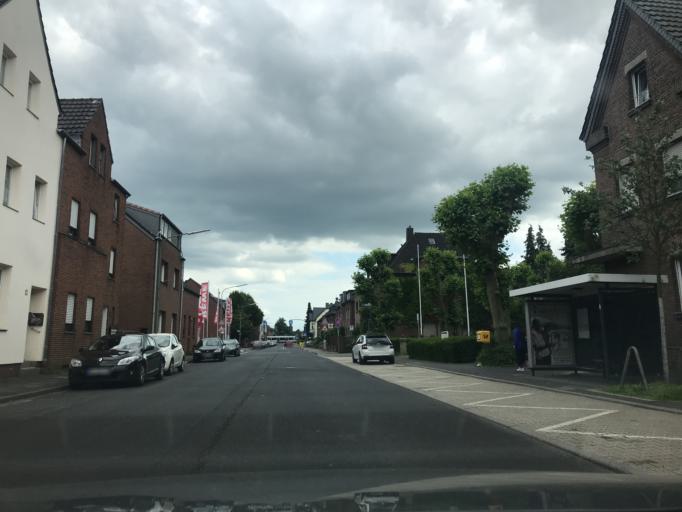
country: DE
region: North Rhine-Westphalia
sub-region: Regierungsbezirk Dusseldorf
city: Neuss
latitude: 51.1673
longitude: 6.6619
